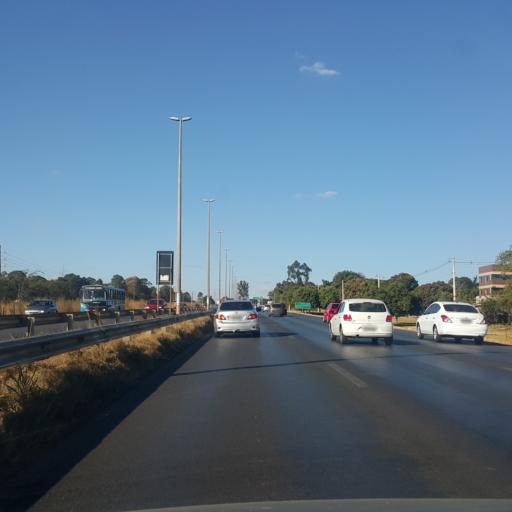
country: BR
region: Federal District
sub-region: Brasilia
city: Brasilia
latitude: -15.7950
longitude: -48.0631
